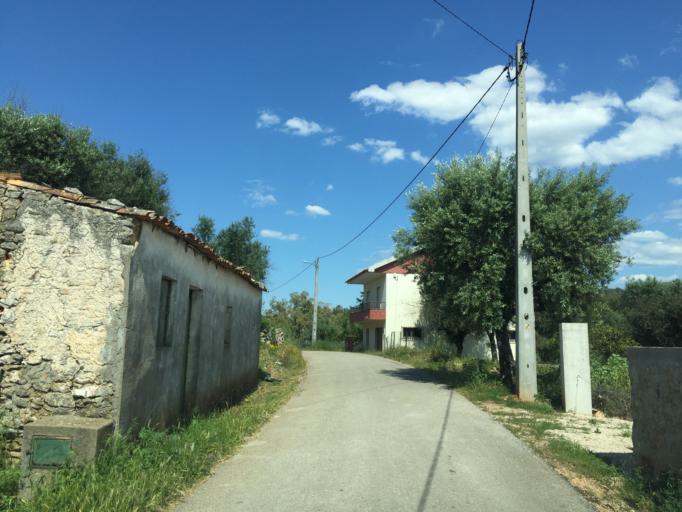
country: PT
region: Leiria
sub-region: Alvaiazere
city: Alvaiazere
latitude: 39.7976
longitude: -8.4316
